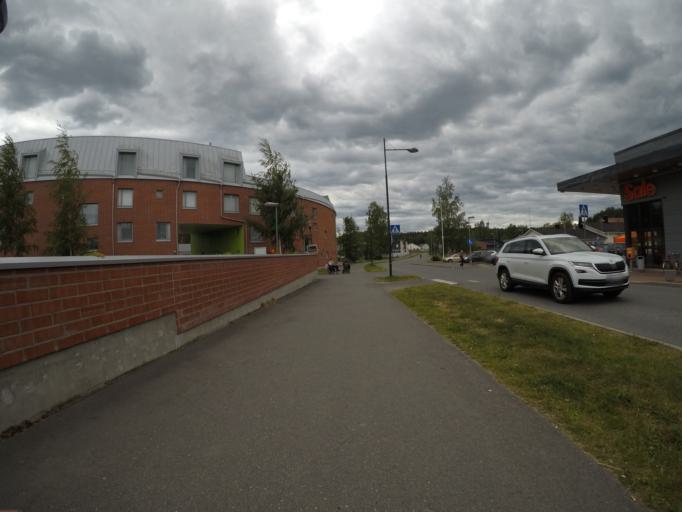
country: FI
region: Haeme
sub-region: Haemeenlinna
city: Haemeenlinna
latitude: 60.9924
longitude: 24.4377
